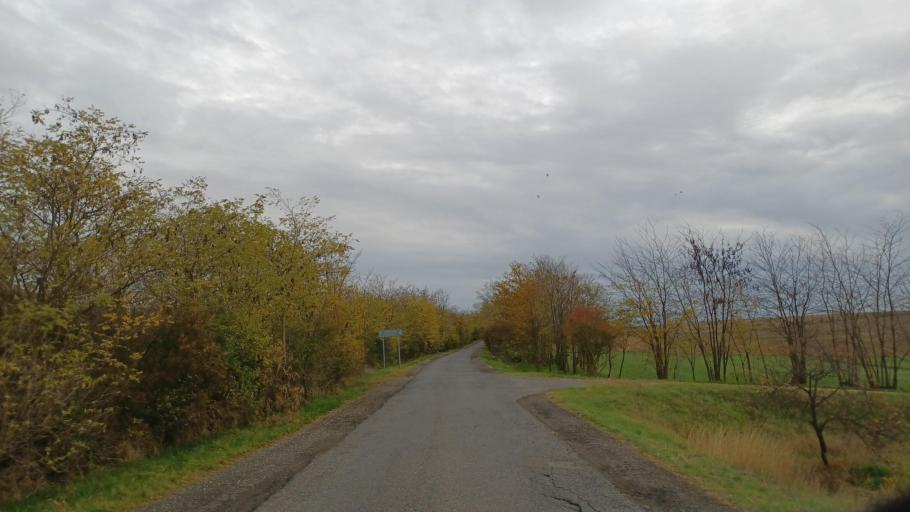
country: HU
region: Tolna
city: Nagydorog
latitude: 46.6838
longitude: 18.5980
